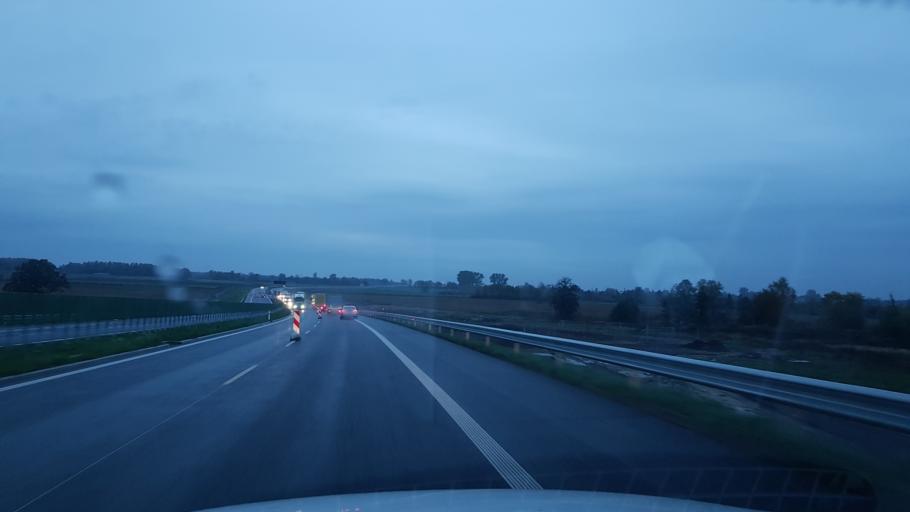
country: PL
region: West Pomeranian Voivodeship
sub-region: Powiat gryficki
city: Ploty
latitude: 53.8003
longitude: 15.2527
